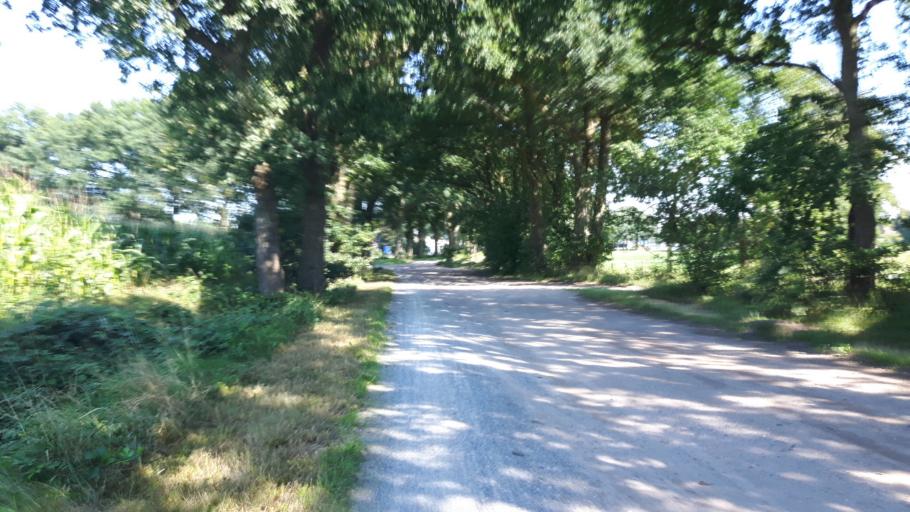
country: NL
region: Drenthe
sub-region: Gemeente Tynaarlo
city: Tynaarlo
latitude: 53.1216
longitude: 6.5983
